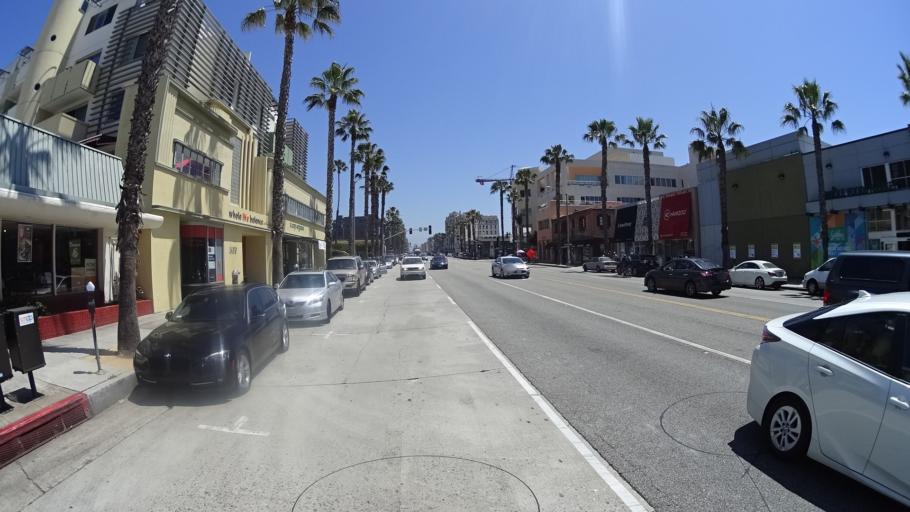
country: US
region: California
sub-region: Los Angeles County
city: Santa Monica
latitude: 34.0200
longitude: -118.4973
